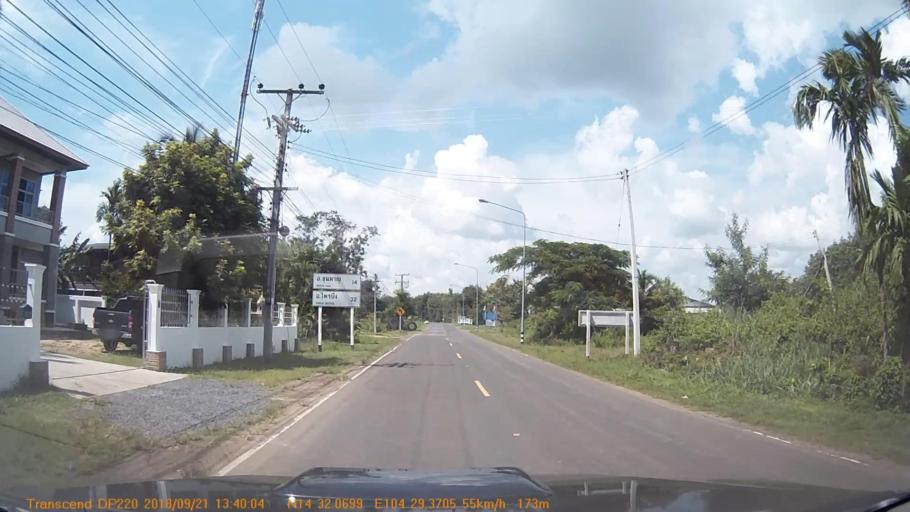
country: TH
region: Sisaket
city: Khun Han
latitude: 14.5348
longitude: 104.4895
